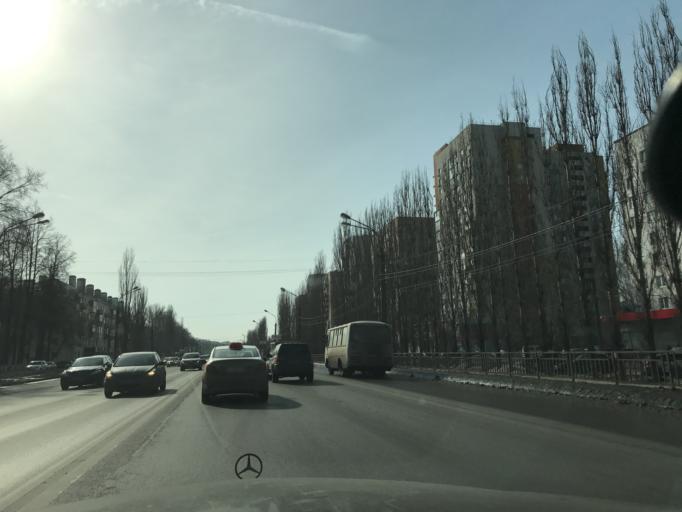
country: RU
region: Nizjnij Novgorod
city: Nizhniy Novgorod
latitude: 56.2737
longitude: 43.9193
